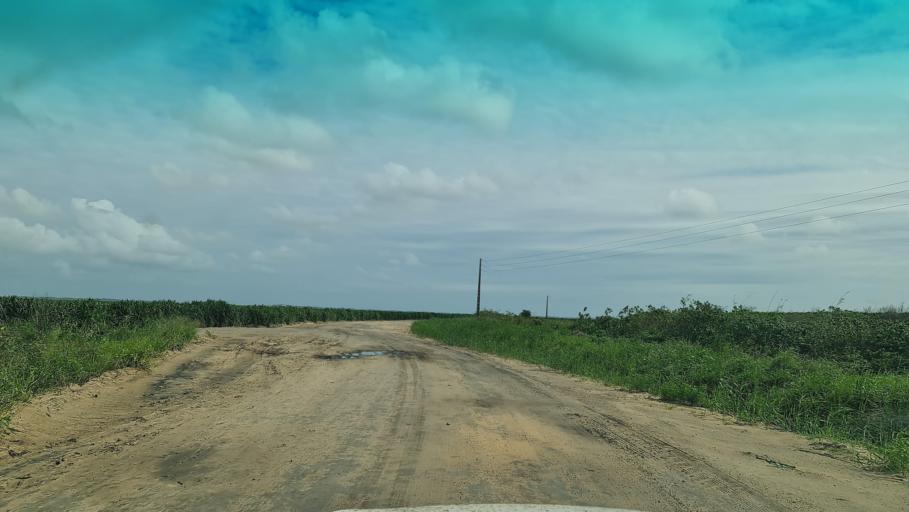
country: MZ
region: Maputo
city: Manhica
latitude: -25.4609
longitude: 32.8186
